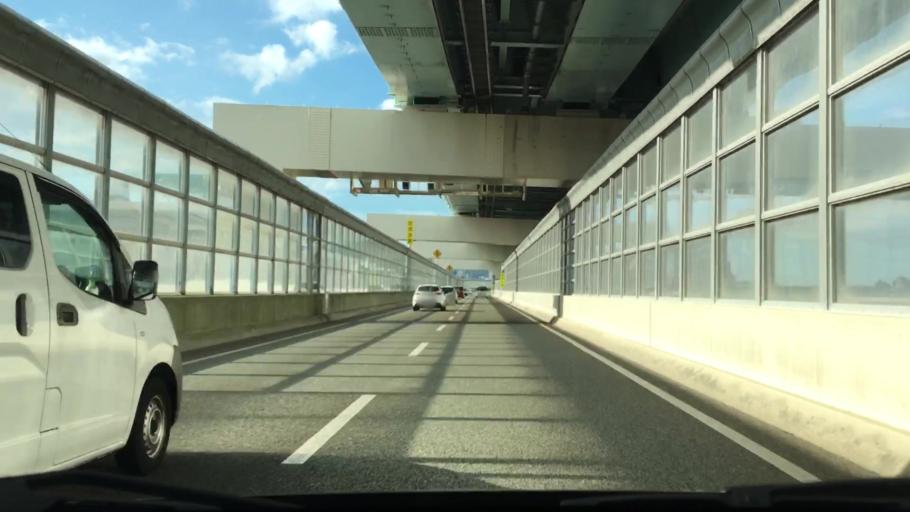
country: JP
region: Fukuoka
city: Fukuoka-shi
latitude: 33.5727
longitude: 130.3165
